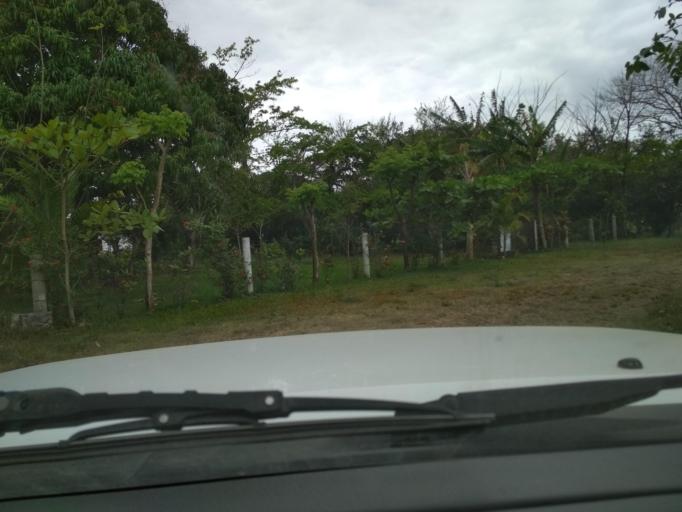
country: MX
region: Veracruz
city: El Tejar
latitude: 19.0721
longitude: -96.1477
